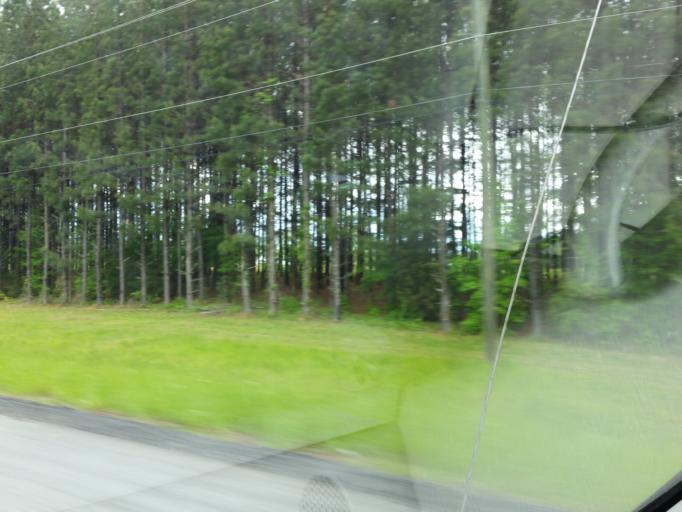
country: US
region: Georgia
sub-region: Spalding County
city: Griffin
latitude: 33.1653
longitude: -84.2592
